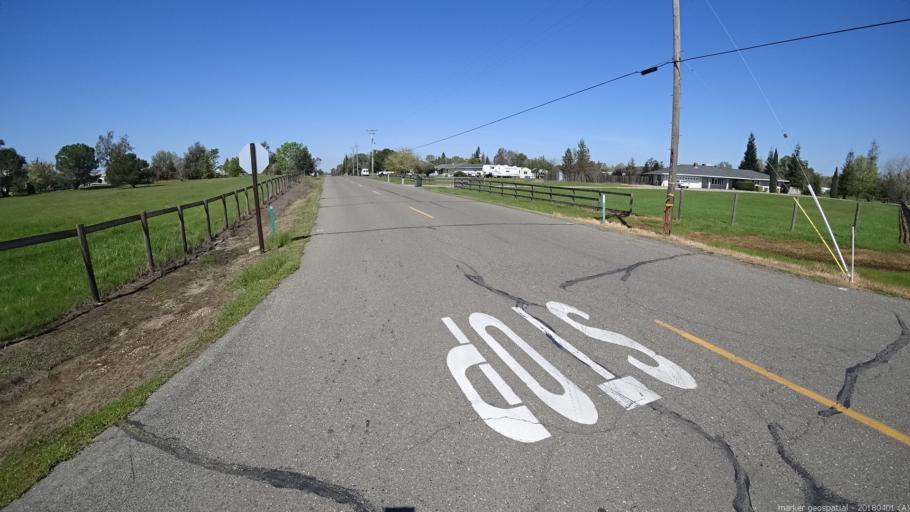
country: US
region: California
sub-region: Sacramento County
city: Wilton
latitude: 38.4140
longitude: -121.2060
